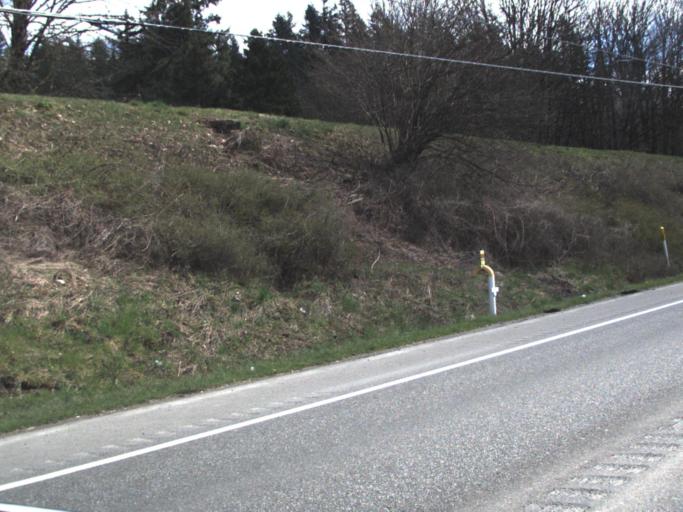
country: US
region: Washington
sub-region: King County
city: Maple Valley
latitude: 47.4121
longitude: -122.0409
